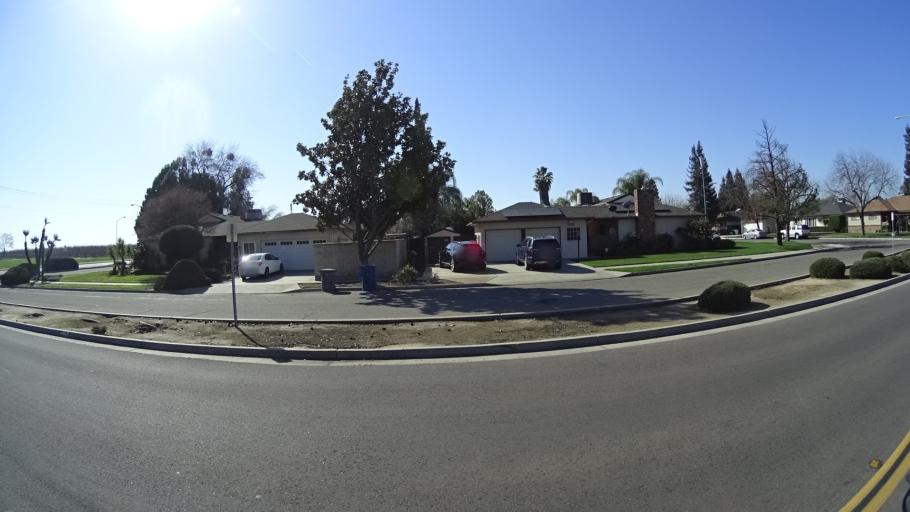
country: US
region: California
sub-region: Fresno County
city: Clovis
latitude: 36.8304
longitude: -119.7549
